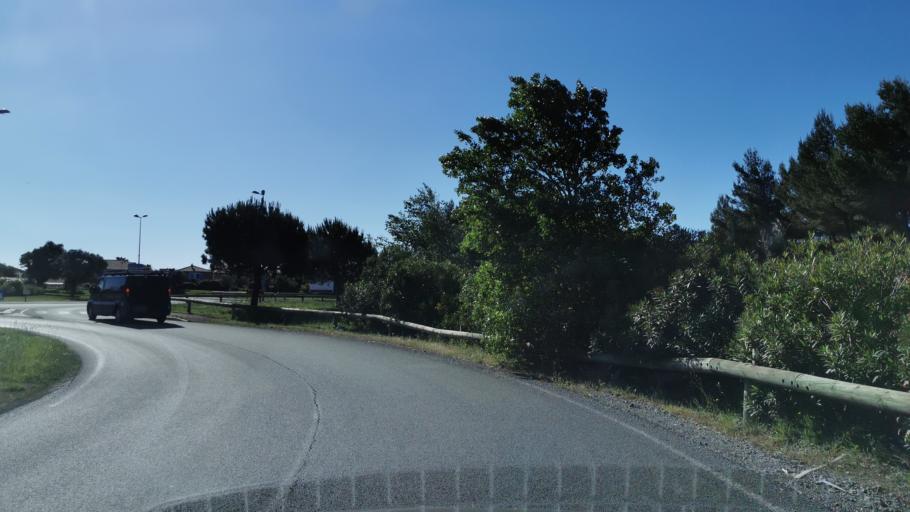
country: FR
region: Languedoc-Roussillon
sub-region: Departement de l'Aude
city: Armissan
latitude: 43.1558
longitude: 3.1551
